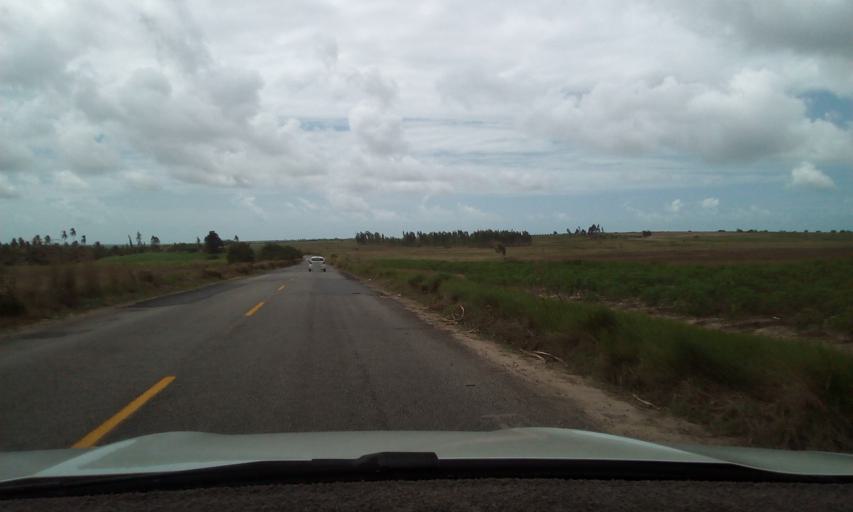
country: BR
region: Paraiba
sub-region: Rio Tinto
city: Rio Tinto
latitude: -6.7785
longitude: -35.0490
